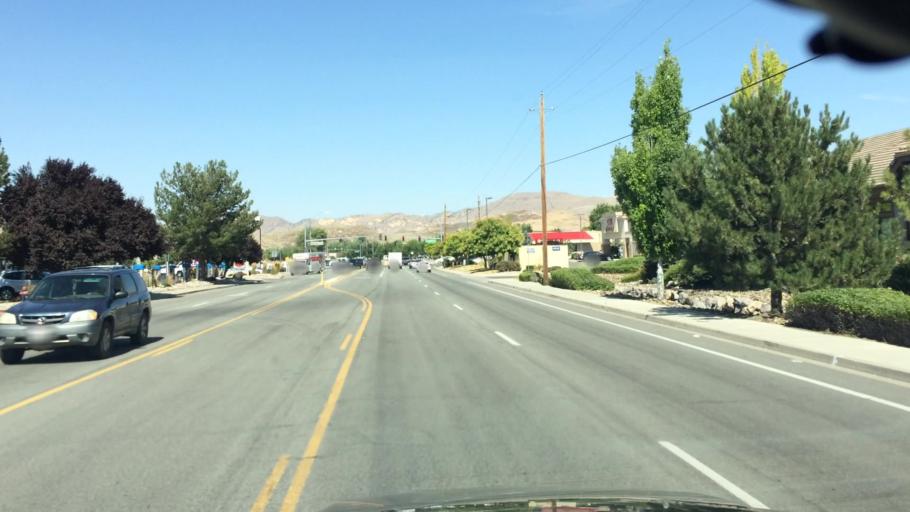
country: US
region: Nevada
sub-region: Washoe County
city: Reno
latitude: 39.4557
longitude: -119.7811
